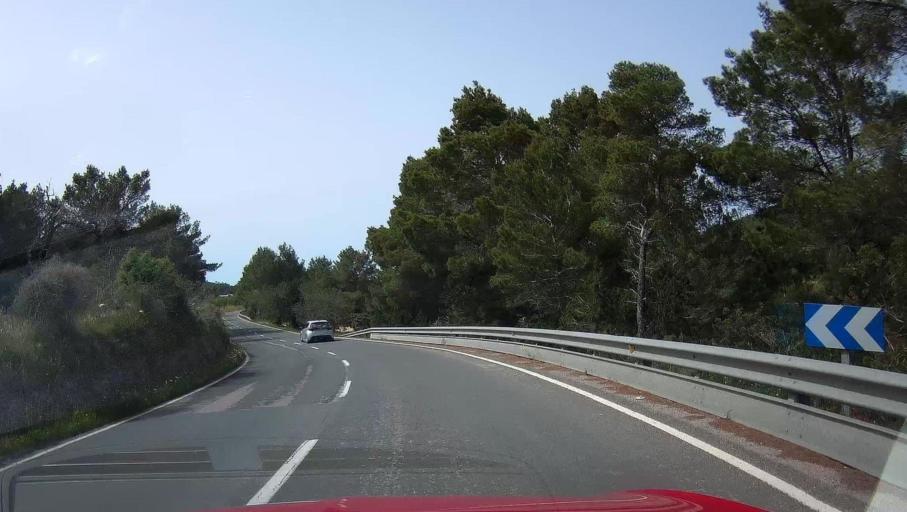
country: ES
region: Balearic Islands
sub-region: Illes Balears
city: Sant Joan de Labritja
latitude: 39.0909
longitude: 1.5027
